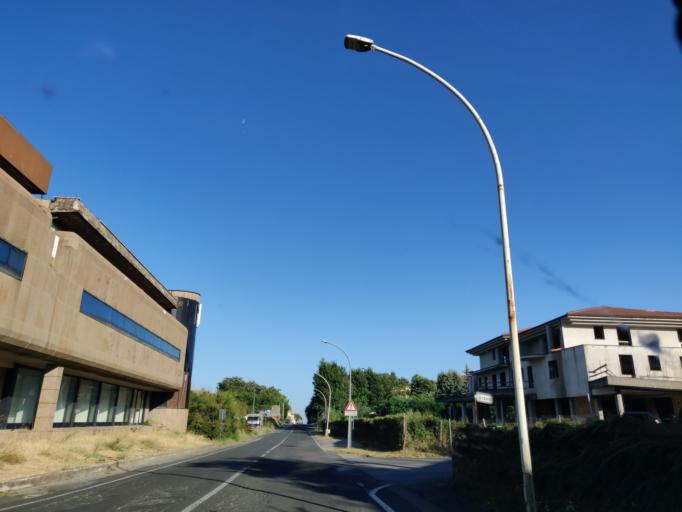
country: IT
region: Tuscany
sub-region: Provincia di Siena
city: Piancastagnaio
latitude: 42.8525
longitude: 11.6865
